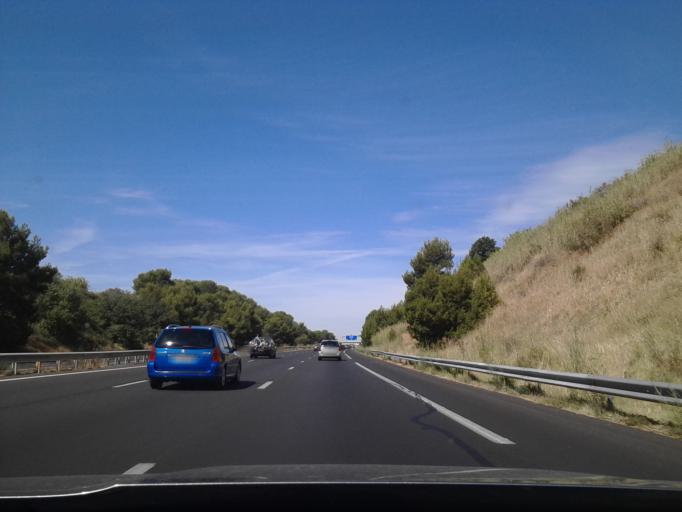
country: FR
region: Languedoc-Roussillon
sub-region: Departement de l'Herault
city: Sauvian
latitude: 43.3051
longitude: 3.2335
